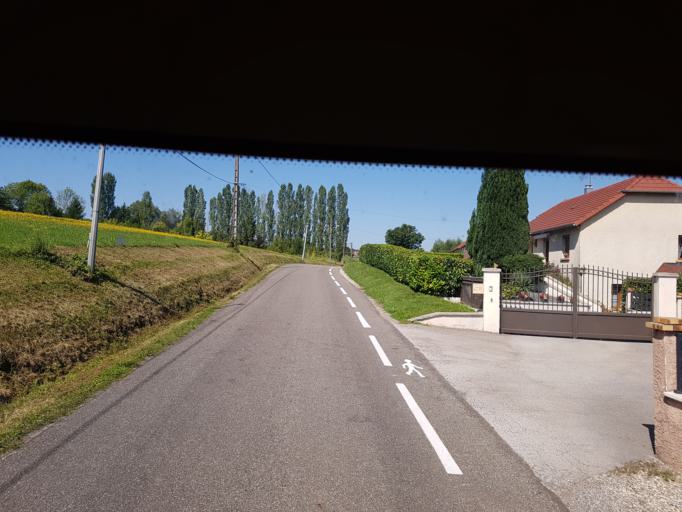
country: FR
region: Franche-Comte
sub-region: Departement du Jura
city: Perrigny
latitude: 46.7296
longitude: 5.5813
